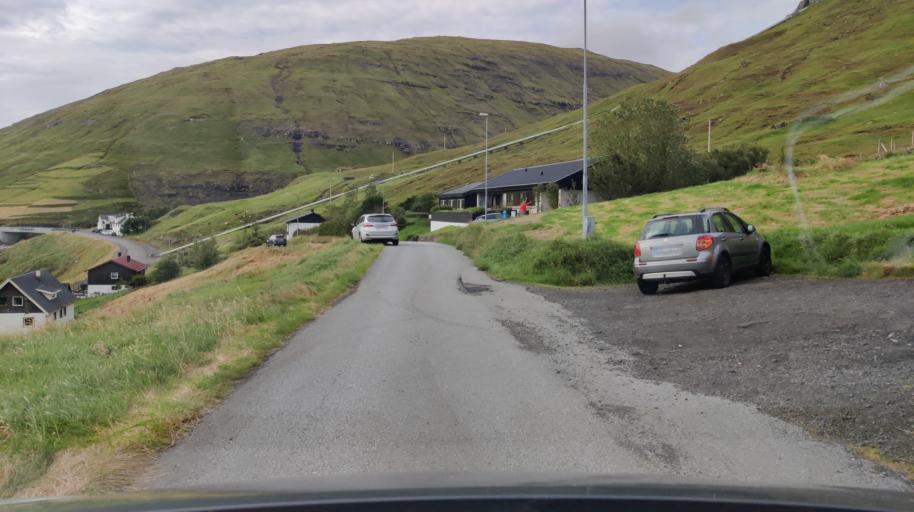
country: FO
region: Streymoy
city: Vestmanna
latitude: 62.1545
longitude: -7.1441
